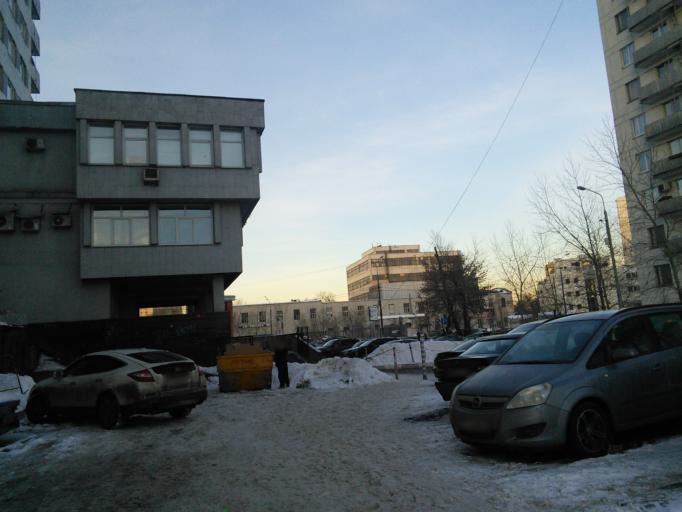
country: RU
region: Moscow
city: Lefortovo
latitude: 55.7701
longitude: 37.6884
